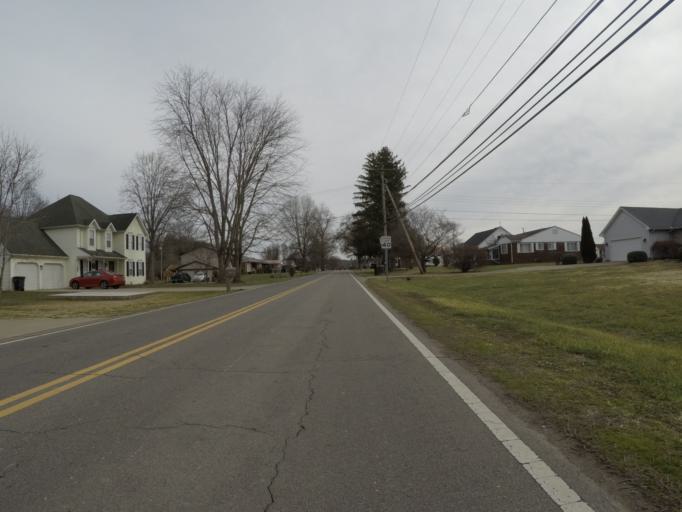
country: US
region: West Virginia
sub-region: Cabell County
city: Pea Ridge
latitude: 38.4540
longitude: -82.3471
